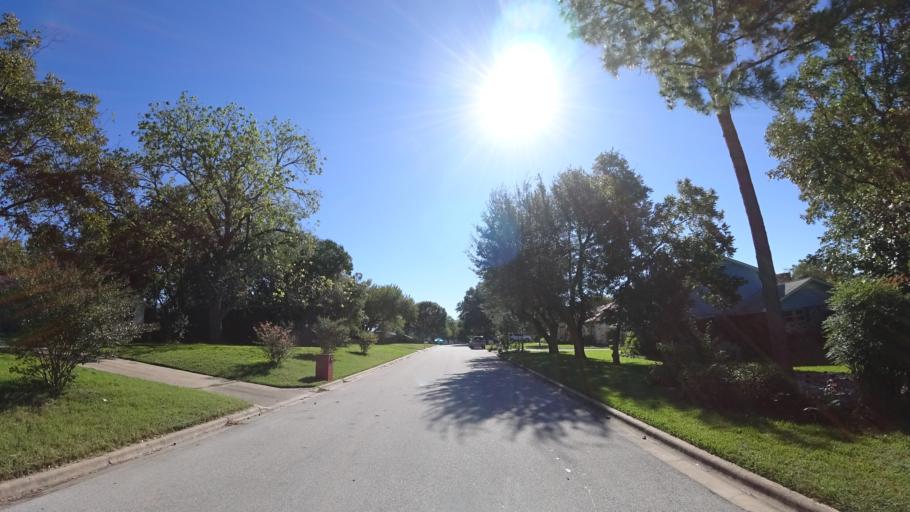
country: US
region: Texas
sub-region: Travis County
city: Manor
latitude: 30.3325
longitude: -97.6533
